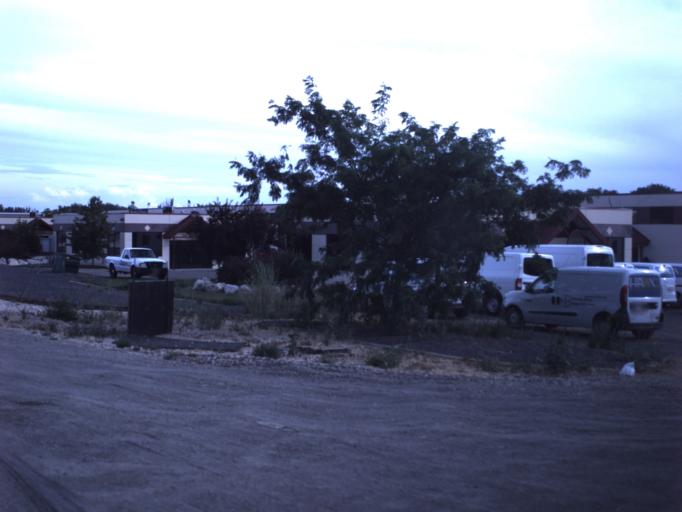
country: US
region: Utah
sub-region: Weber County
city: Farr West
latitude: 41.3255
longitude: -112.0321
